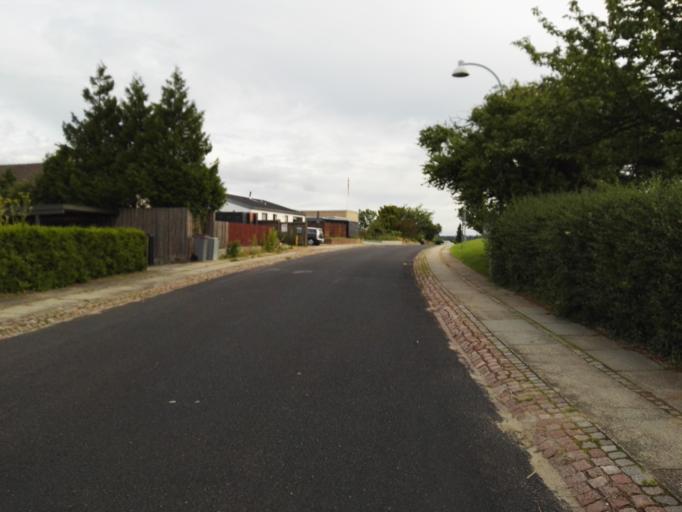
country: DK
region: Capital Region
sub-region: Ballerup Kommune
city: Malov
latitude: 55.7548
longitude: 12.3191
